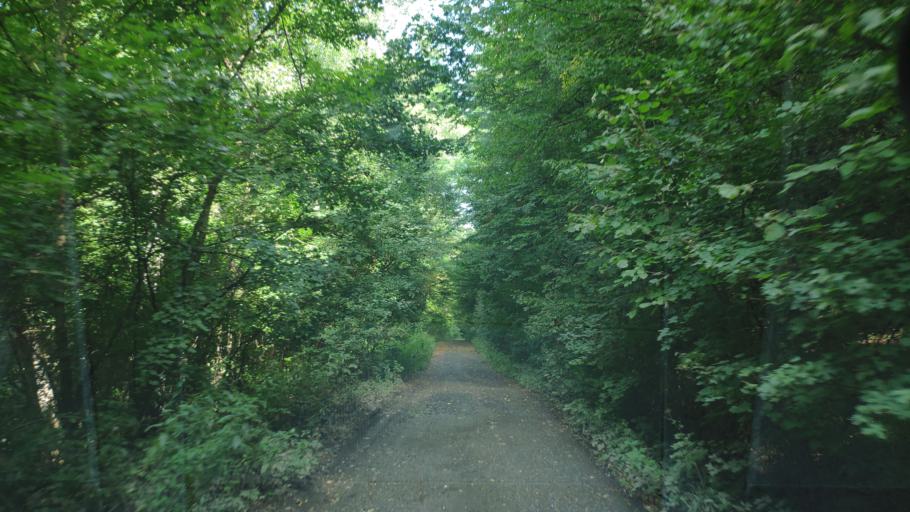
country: HU
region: Borsod-Abauj-Zemplen
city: Putnok
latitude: 48.4512
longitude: 20.3786
